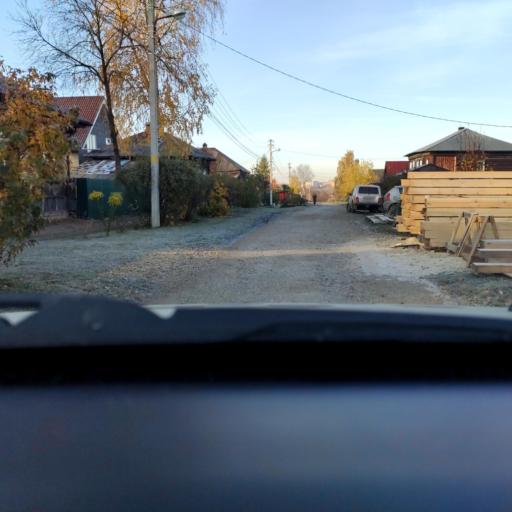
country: RU
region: Perm
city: Perm
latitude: 58.0266
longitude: 56.3252
